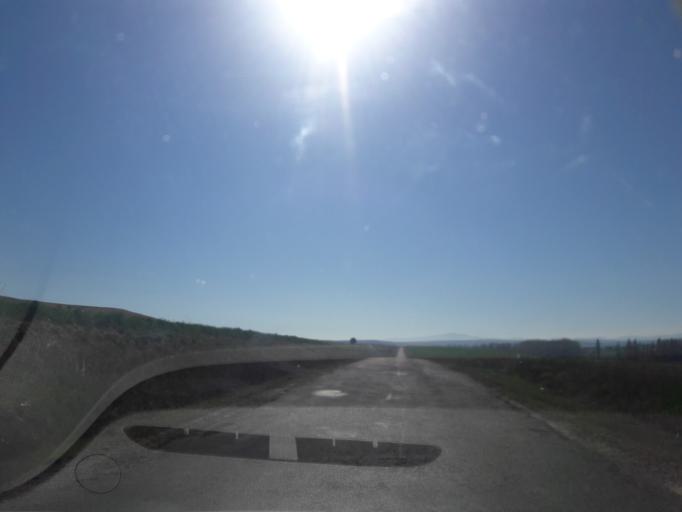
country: ES
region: Castille and Leon
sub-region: Provincia de Salamanca
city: Mancera de Abajo
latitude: 40.8291
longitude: -5.1854
